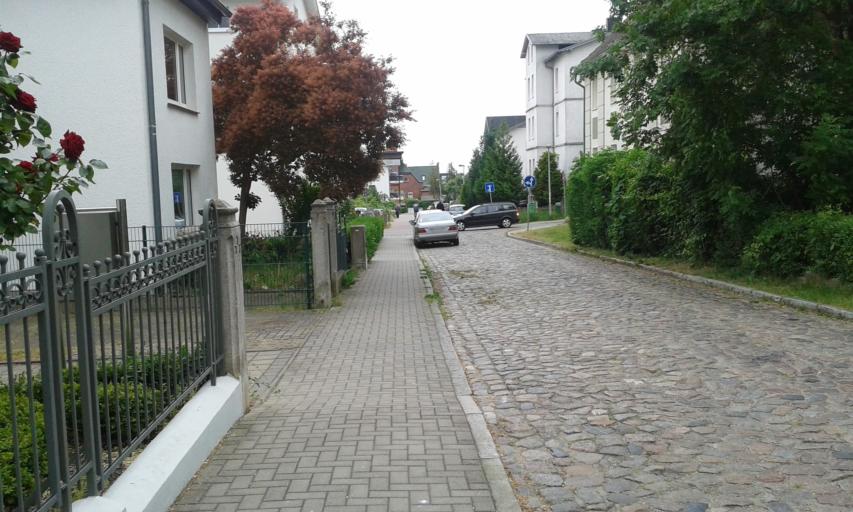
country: DE
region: Mecklenburg-Vorpommern
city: Sassnitz
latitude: 54.5173
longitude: 13.6478
